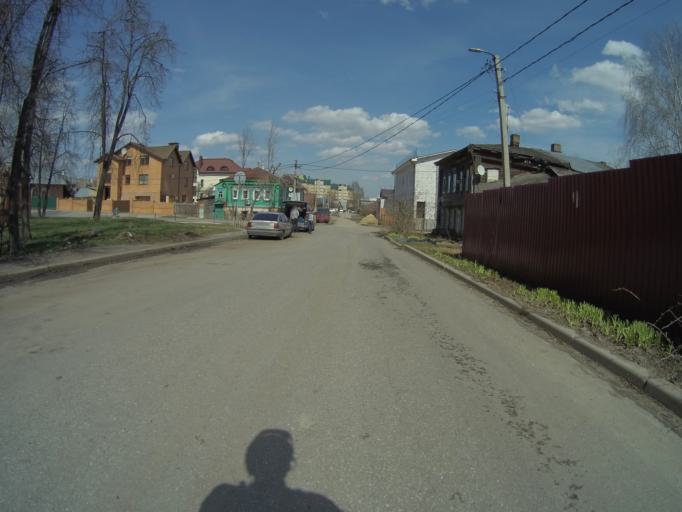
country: RU
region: Vladimir
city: Vladimir
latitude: 56.1268
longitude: 40.3762
